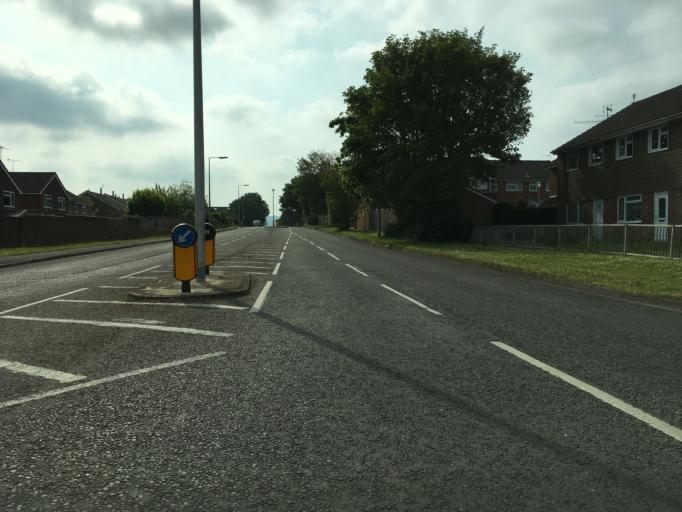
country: GB
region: England
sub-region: North Somerset
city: Nailsea
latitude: 51.4273
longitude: -2.7617
